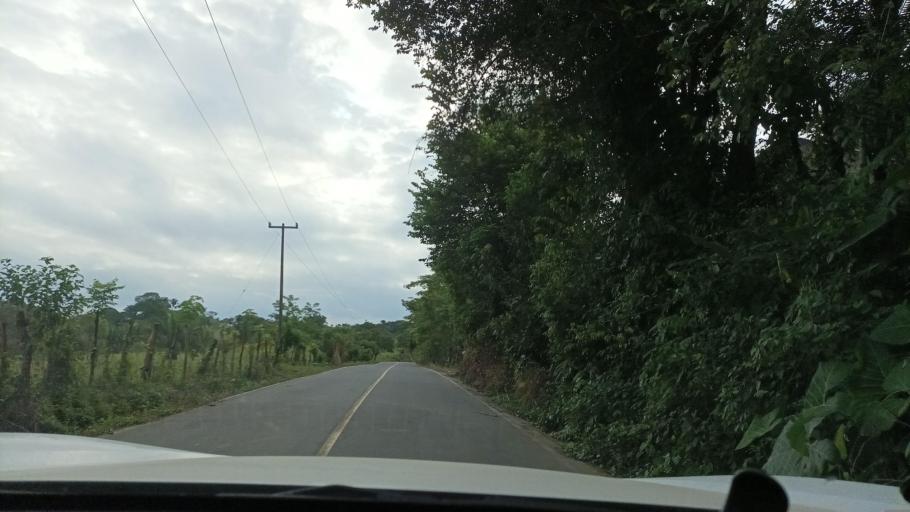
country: MX
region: Veracruz
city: Hidalgotitlan
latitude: 17.7488
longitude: -94.4953
